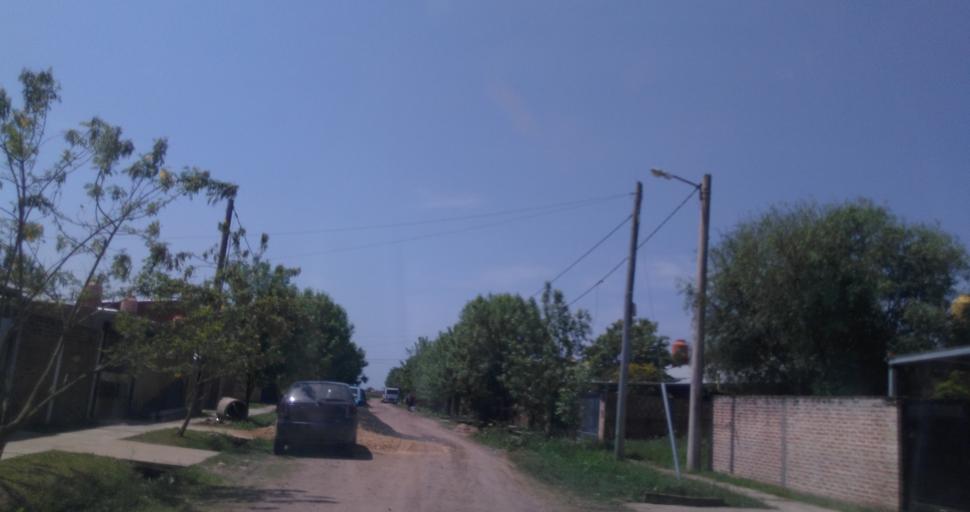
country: AR
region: Chaco
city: Fontana
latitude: -27.3968
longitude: -59.0014
